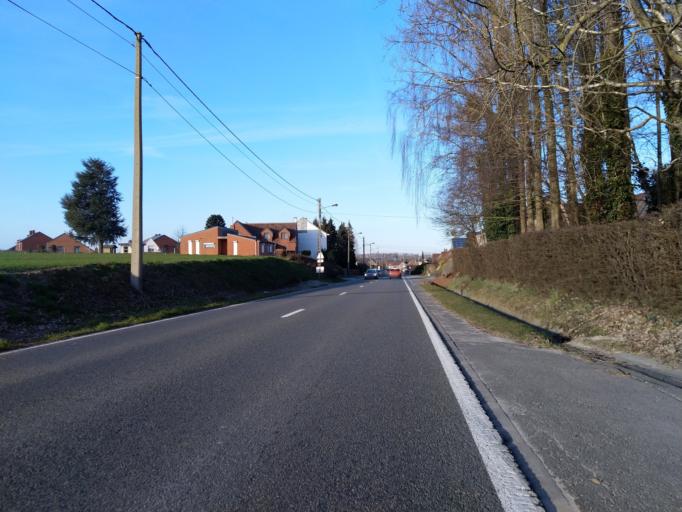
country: BE
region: Wallonia
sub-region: Province du Hainaut
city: Frameries
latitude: 50.3985
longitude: 3.9159
